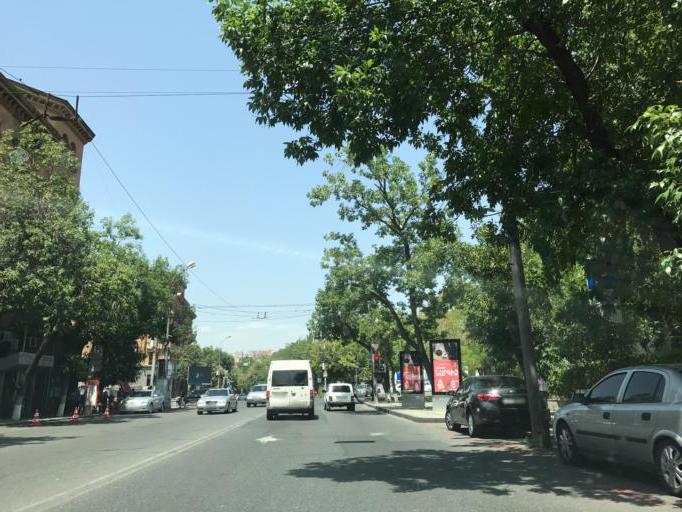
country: AM
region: Yerevan
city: Yerevan
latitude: 40.1854
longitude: 44.5222
